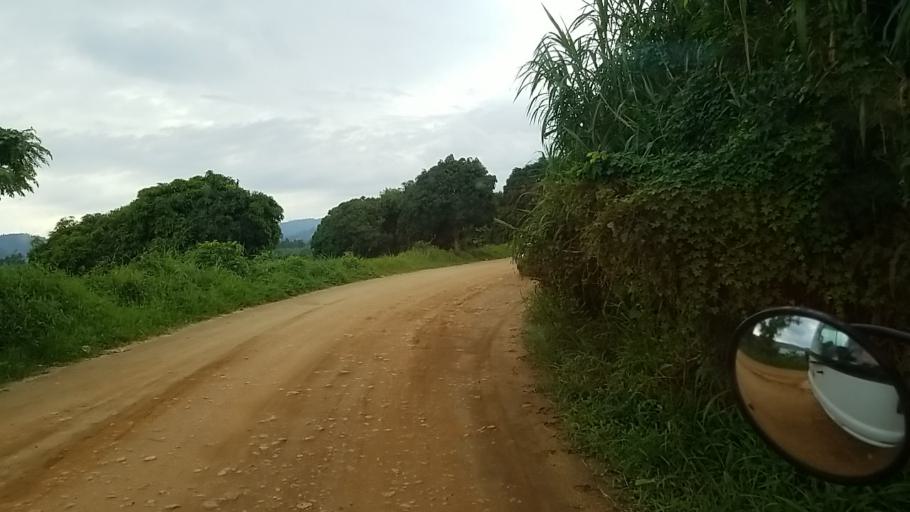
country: CD
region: Nord Kivu
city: Sake
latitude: -1.6750
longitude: 29.0180
